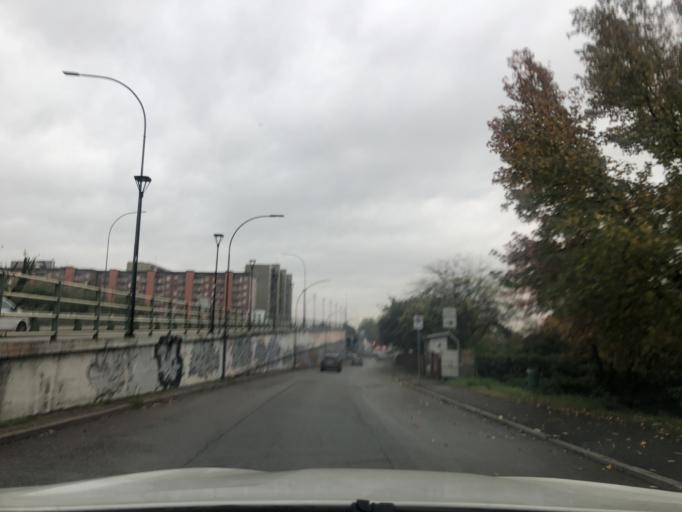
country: IT
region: Lombardy
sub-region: Citta metropolitana di Milano
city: Cesano Boscone
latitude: 45.4395
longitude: 9.1041
